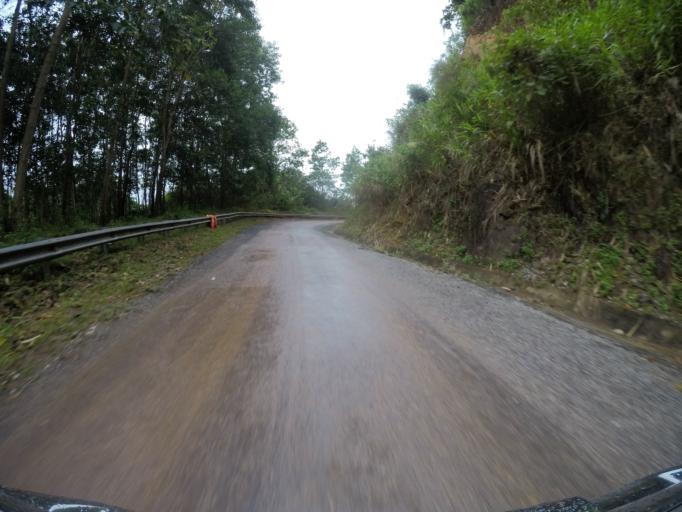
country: LA
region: Xekong
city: Dak Cheung
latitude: 15.6020
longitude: 107.4494
